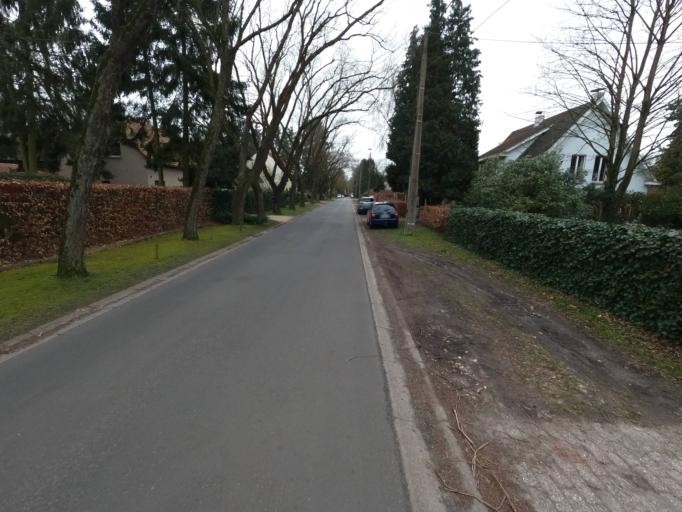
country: BE
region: Flanders
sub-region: Provincie Antwerpen
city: Kalmthout
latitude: 51.3746
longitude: 4.4635
